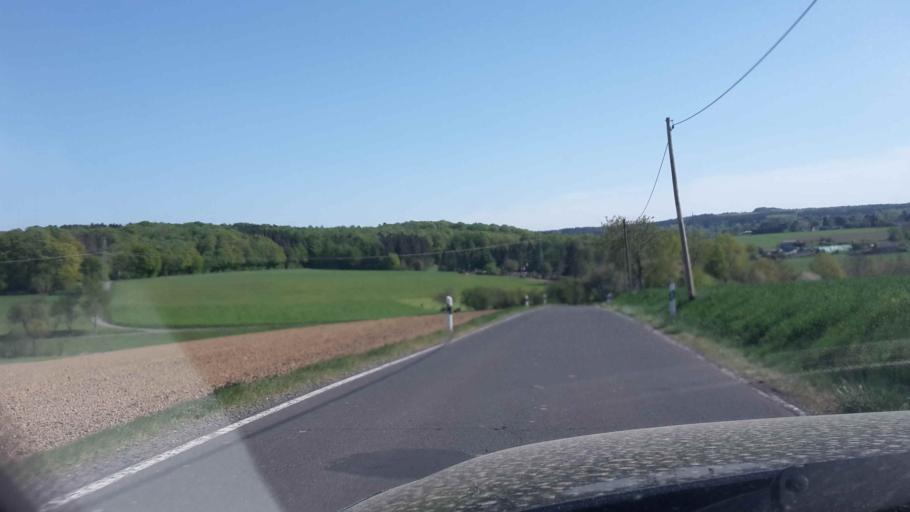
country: DE
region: Rheinland-Pfalz
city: Windhagen
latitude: 50.6827
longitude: 7.3365
